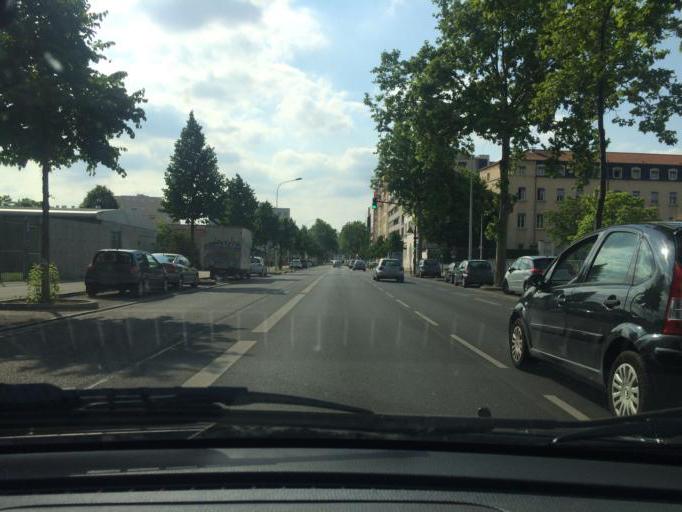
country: FR
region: Rhone-Alpes
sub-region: Departement du Rhone
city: Lyon
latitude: 45.7457
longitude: 4.8708
